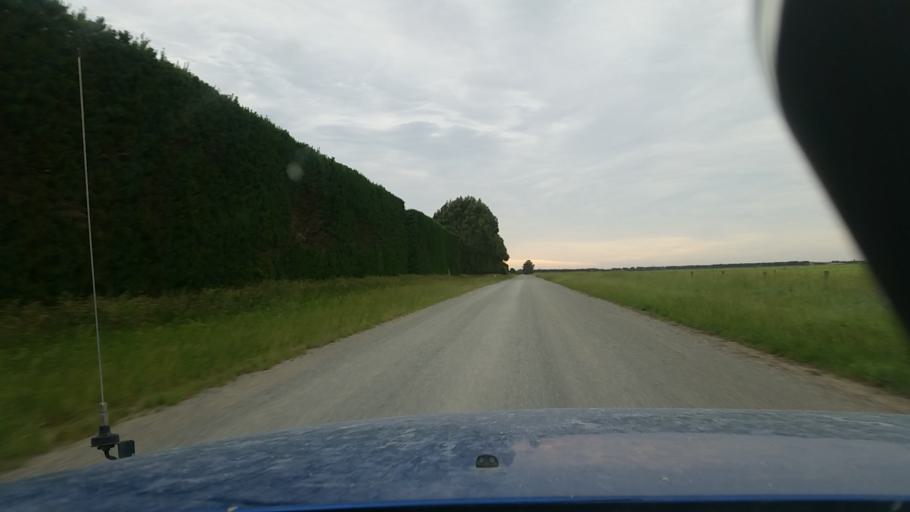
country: NZ
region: Canterbury
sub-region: Ashburton District
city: Tinwald
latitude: -43.9800
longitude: 171.5191
